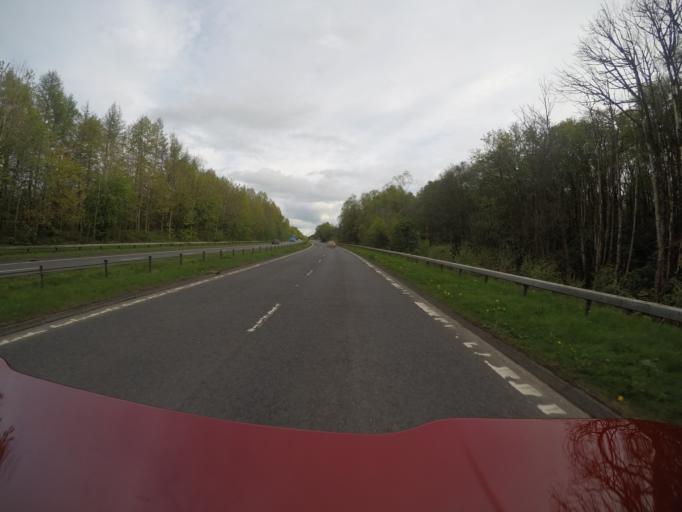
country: GB
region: Scotland
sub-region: West Dunbartonshire
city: Alexandria
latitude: 55.9923
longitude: -4.5939
